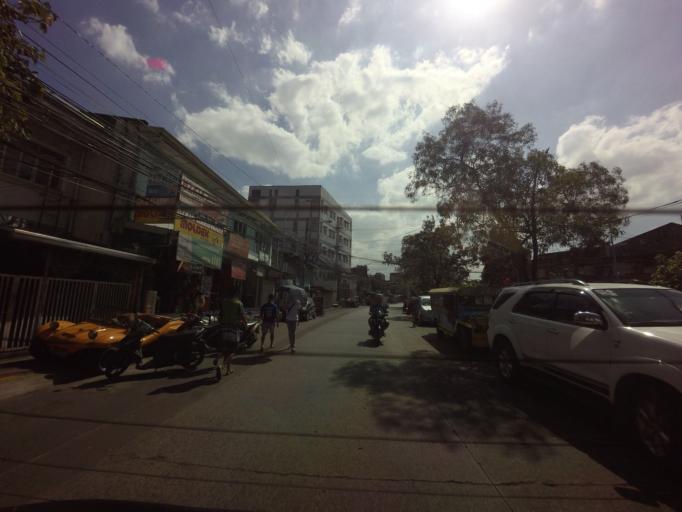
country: PH
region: Metro Manila
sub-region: City of Manila
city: Manila
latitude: 14.6146
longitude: 121.0018
